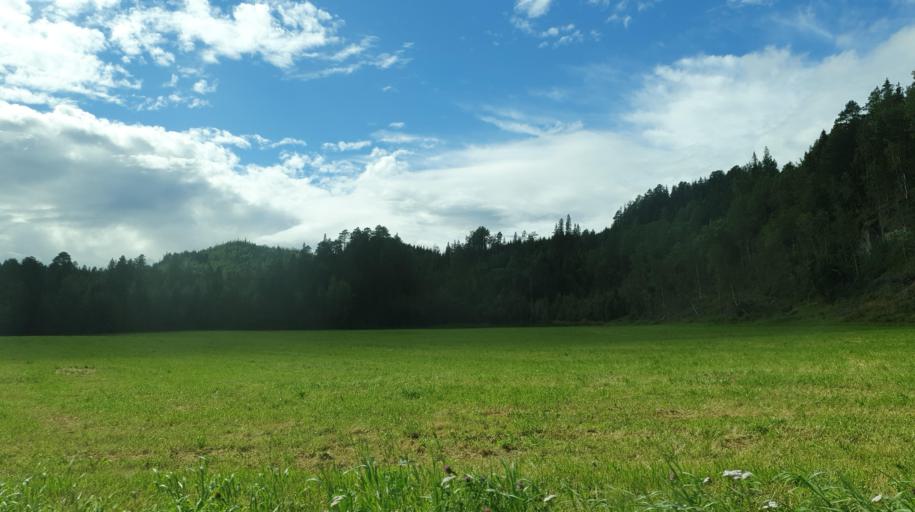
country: NO
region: Nord-Trondelag
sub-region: Levanger
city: Skogn
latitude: 63.5961
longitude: 11.2676
